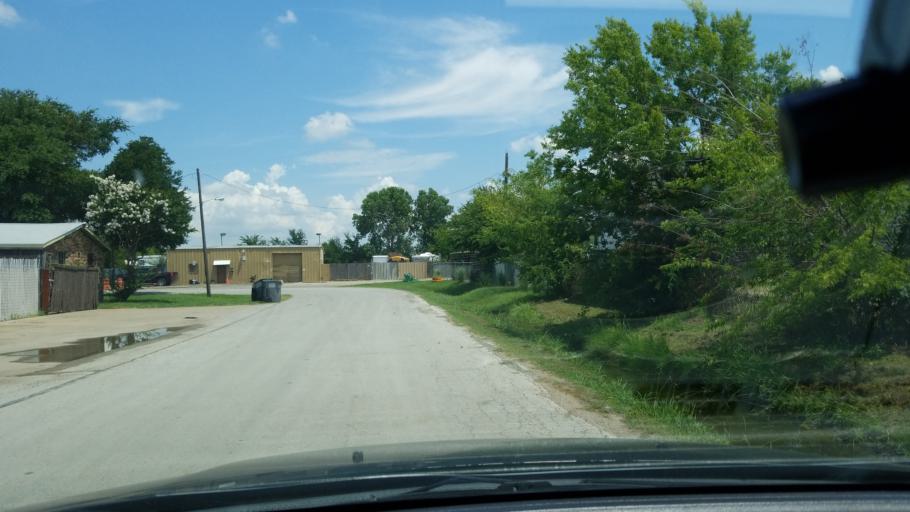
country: US
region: Texas
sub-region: Dallas County
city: Balch Springs
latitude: 32.7440
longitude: -96.6274
